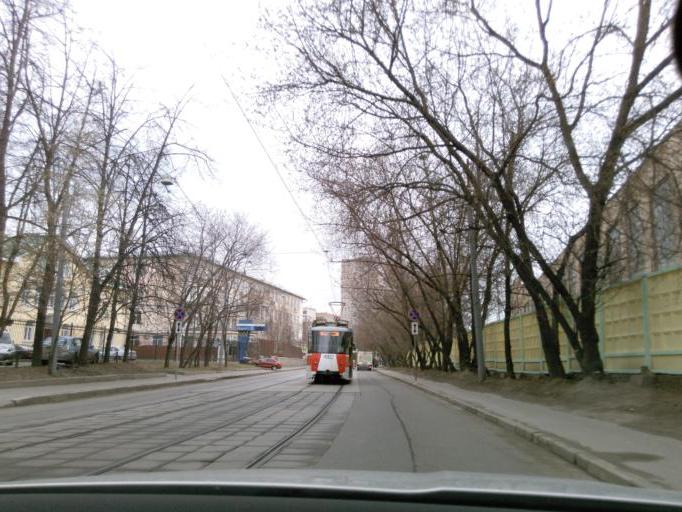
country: RU
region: Moscow
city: Zamoskvorech'ye
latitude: 55.7146
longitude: 37.6335
